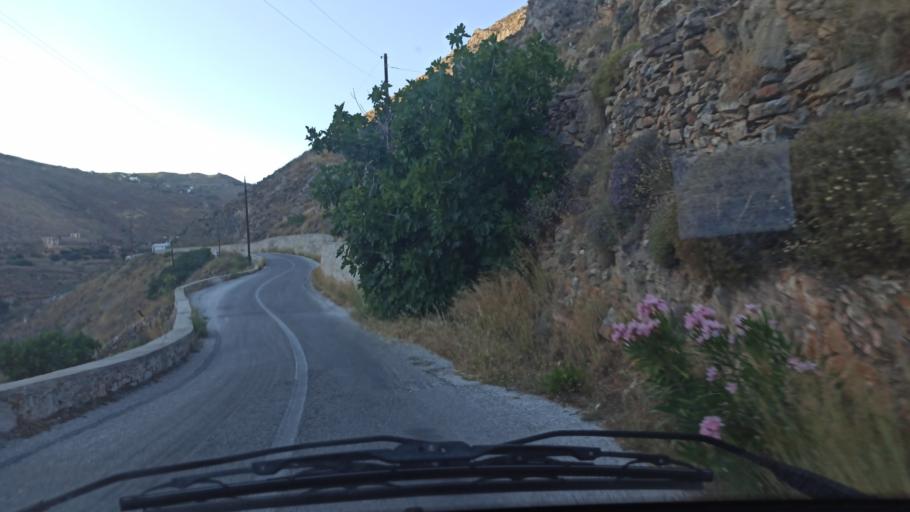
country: GR
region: South Aegean
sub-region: Nomos Kykladon
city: Ano Syros
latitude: 37.4549
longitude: 24.9335
